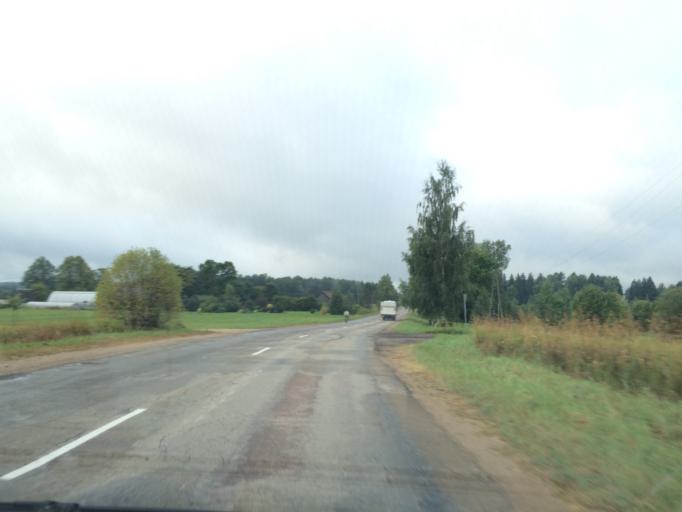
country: LV
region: Ikskile
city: Ikskile
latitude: 56.8625
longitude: 24.5577
